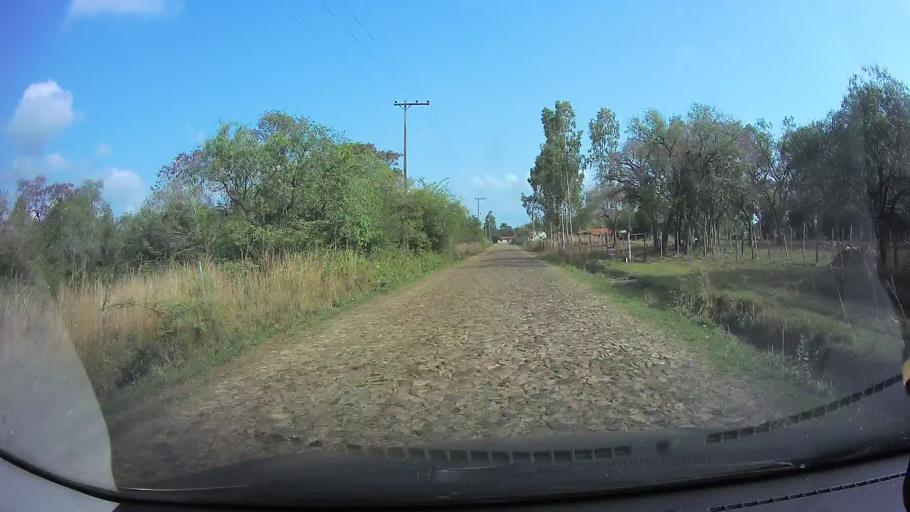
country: PY
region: Cordillera
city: Arroyos y Esteros
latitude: -24.9940
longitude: -57.1933
